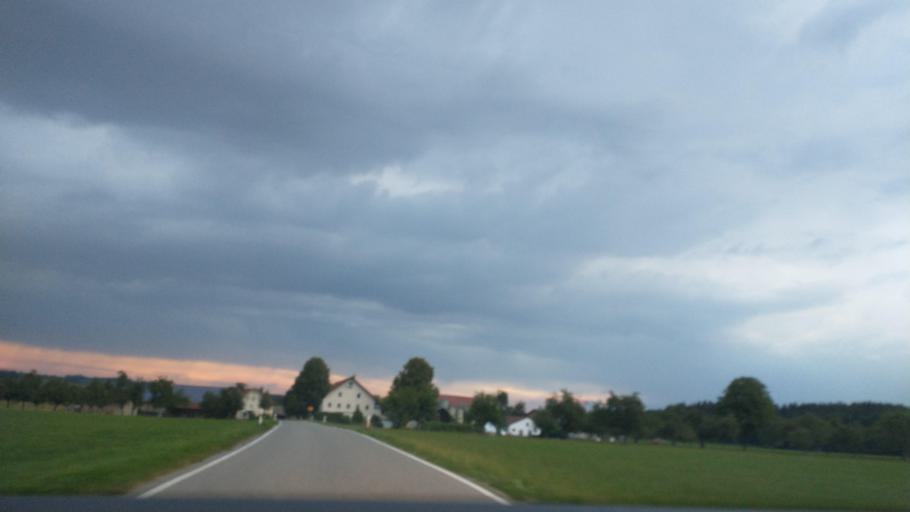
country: DE
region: Baden-Wuerttemberg
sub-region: Tuebingen Region
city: Amtzell
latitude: 47.6849
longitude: 9.7387
